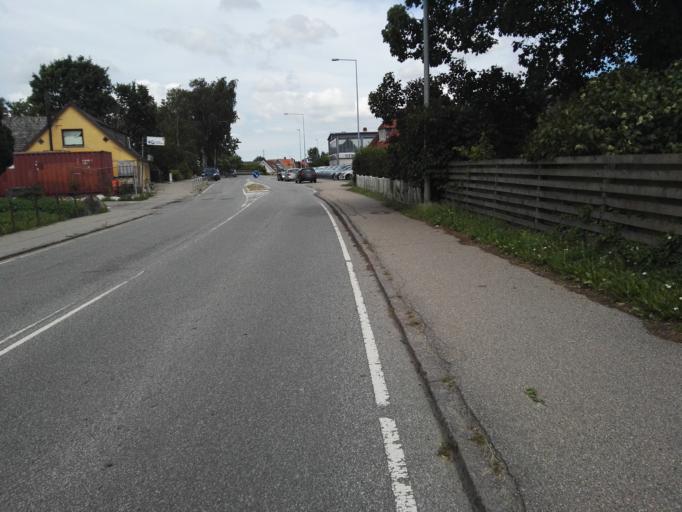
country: DK
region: Capital Region
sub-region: Frederikssund Kommune
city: Slangerup
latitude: 55.8859
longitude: 12.1975
